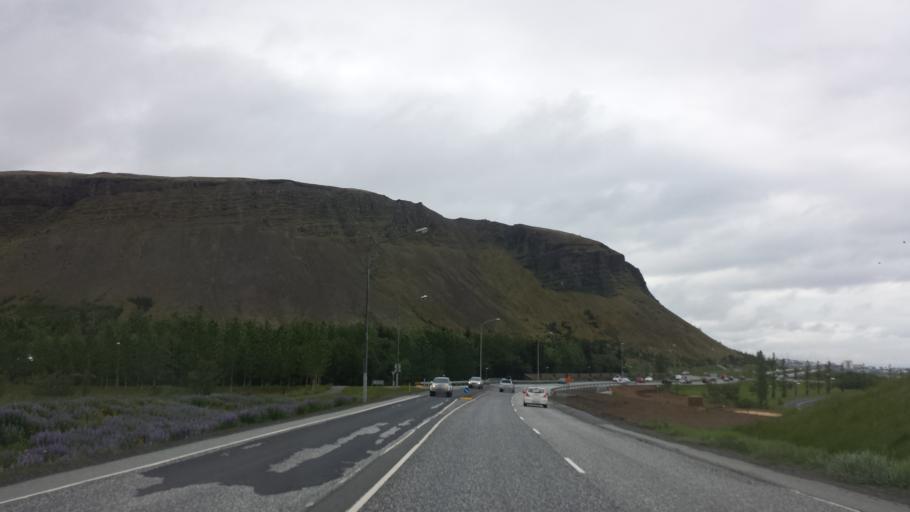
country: IS
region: Capital Region
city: Mosfellsbaer
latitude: 64.1617
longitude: -21.7187
